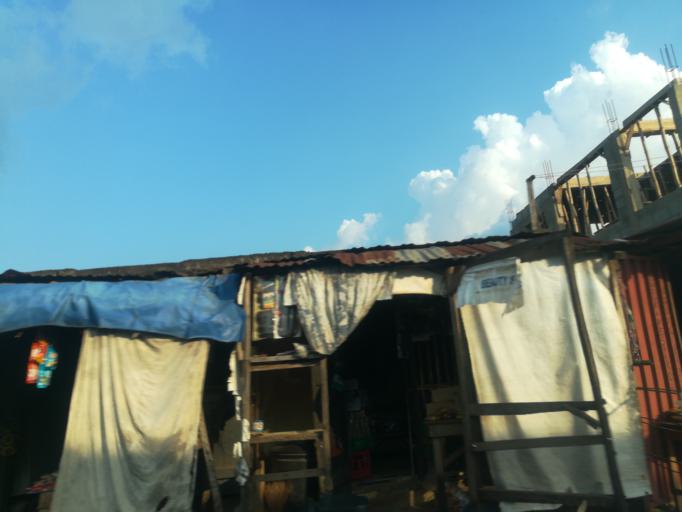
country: NG
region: Oyo
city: Moniya
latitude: 7.4562
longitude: 3.9165
